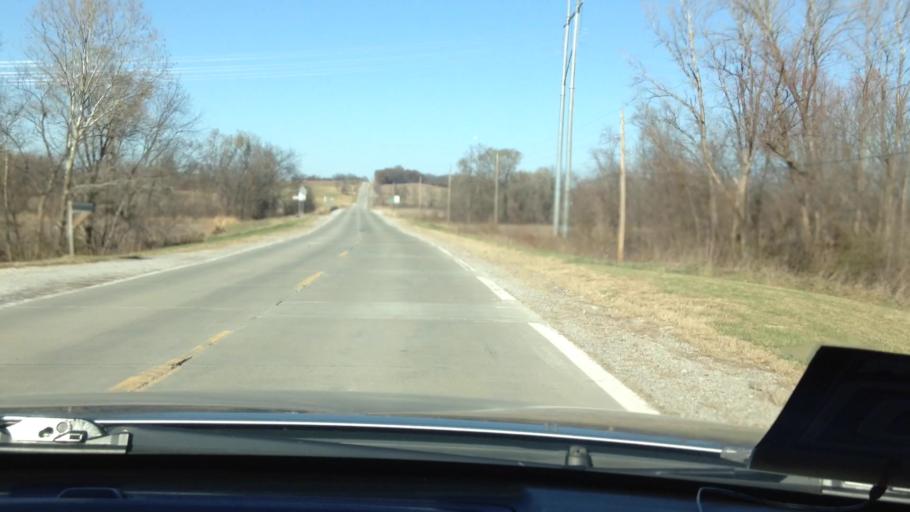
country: US
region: Missouri
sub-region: Platte County
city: Platte City
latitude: 39.5045
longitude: -94.7994
